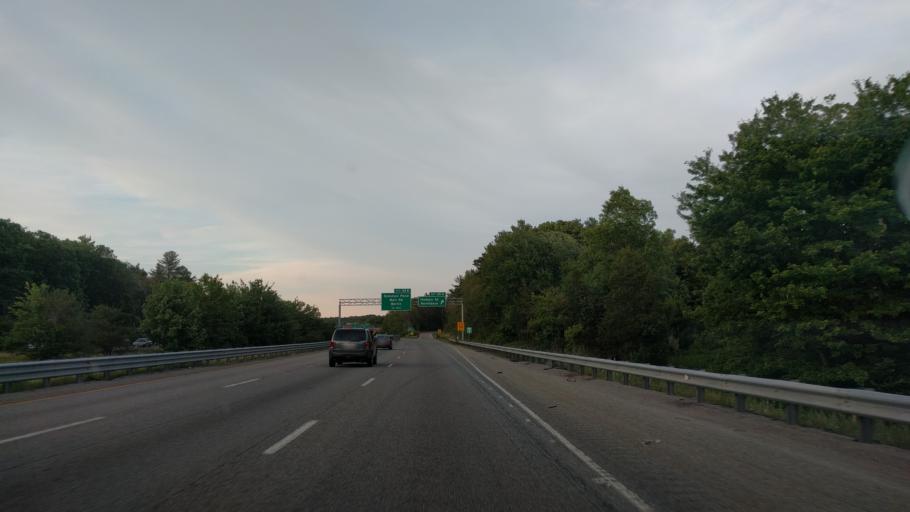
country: US
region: Massachusetts
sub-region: Worcester County
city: Northborough
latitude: 42.3440
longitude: -71.6305
